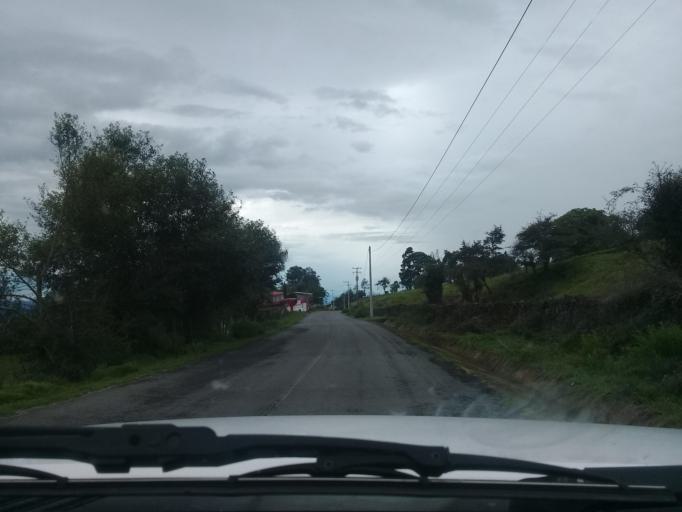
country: MX
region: Veracruz
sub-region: Acajete
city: La Joya
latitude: 19.6154
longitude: -97.0106
